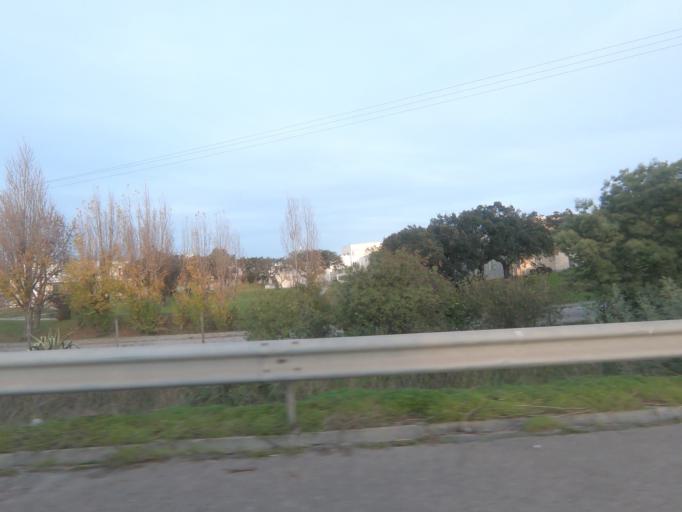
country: PT
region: Setubal
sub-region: Setubal
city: Setubal
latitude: 38.5225
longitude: -8.8426
